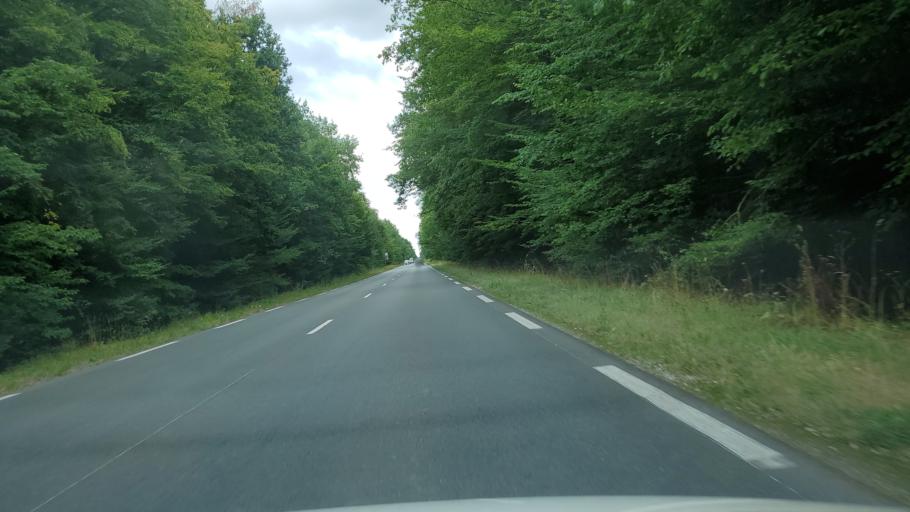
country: FR
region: Ile-de-France
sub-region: Departement de Seine-et-Marne
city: Mortcerf
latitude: 48.7661
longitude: 2.9180
